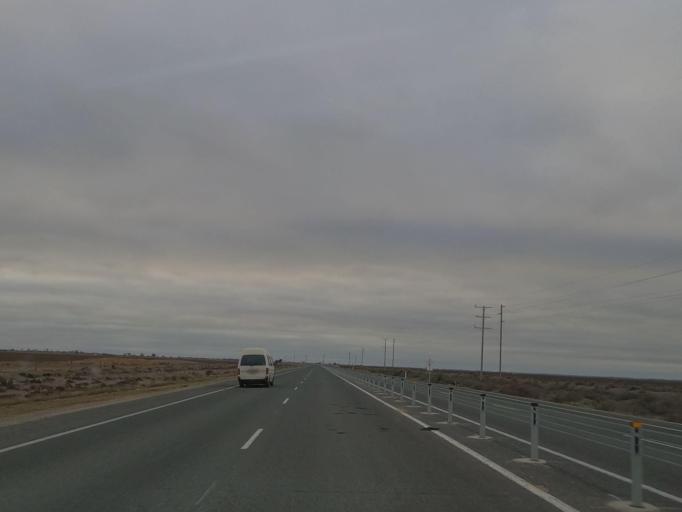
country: AU
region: Victoria
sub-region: Swan Hill
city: Swan Hill
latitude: -35.5142
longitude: 143.7268
